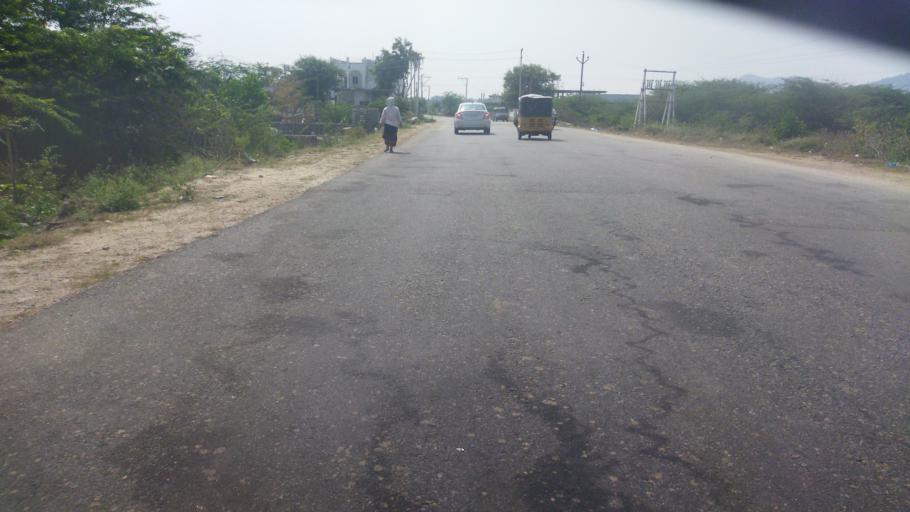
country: IN
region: Telangana
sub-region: Nalgonda
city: Nalgonda
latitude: 17.0805
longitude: 79.2837
